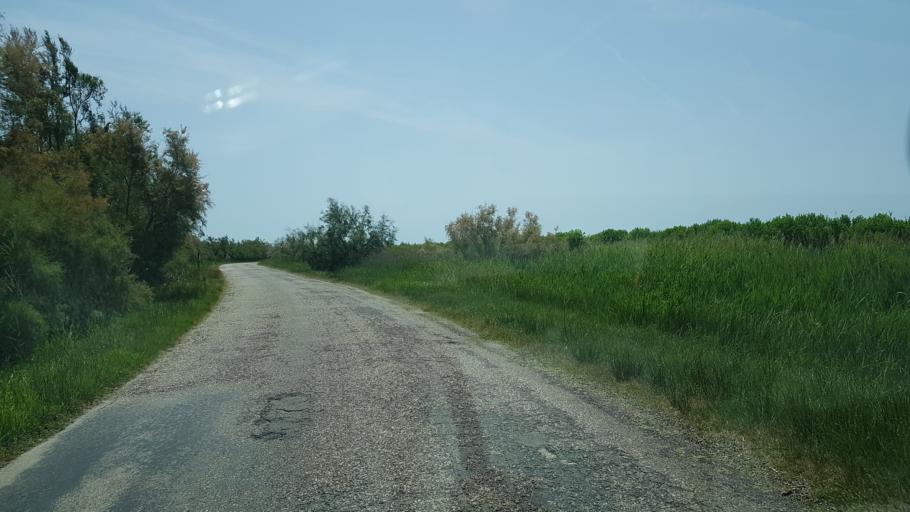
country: FR
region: Provence-Alpes-Cote d'Azur
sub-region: Departement des Bouches-du-Rhone
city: Arles
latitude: 43.5536
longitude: 4.6261
